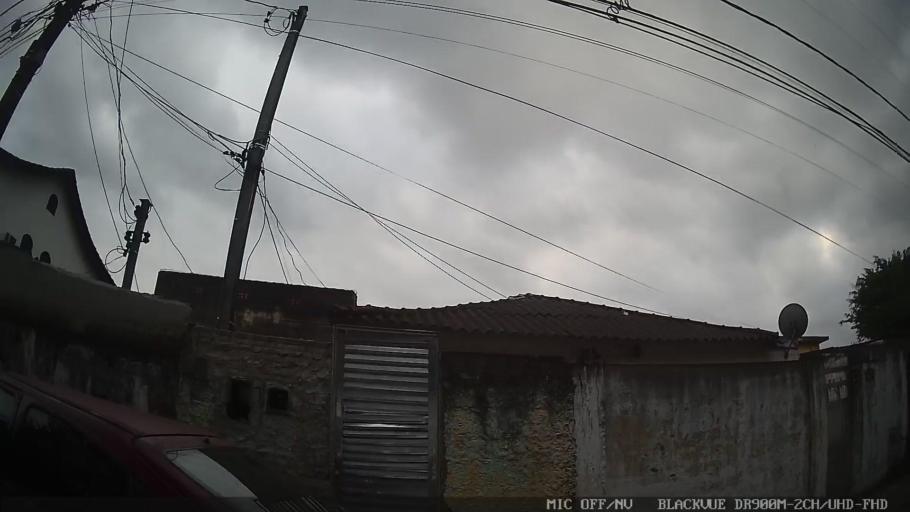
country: BR
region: Sao Paulo
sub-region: Santos
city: Santos
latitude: -23.9475
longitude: -46.2879
